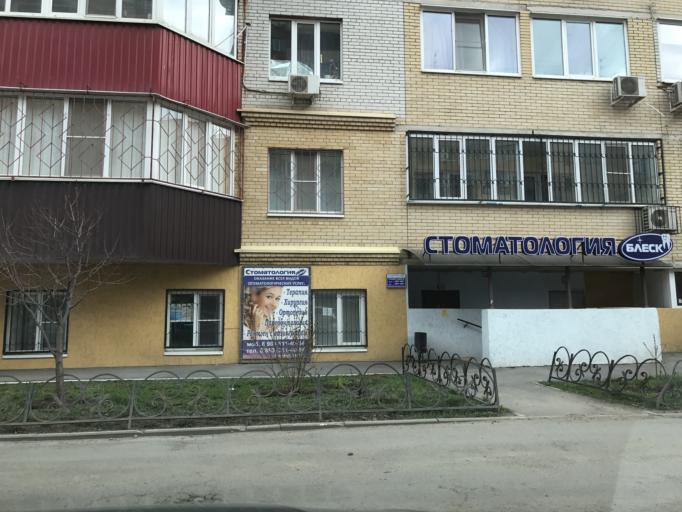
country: RU
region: Rostov
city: Rostov-na-Donu
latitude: 47.2164
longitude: 39.6195
